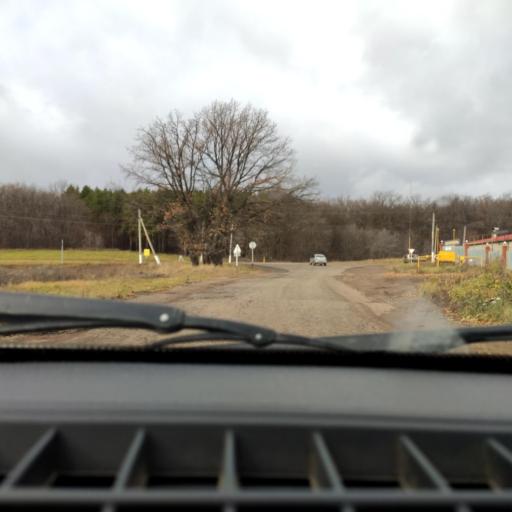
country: RU
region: Bashkortostan
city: Mikhaylovka
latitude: 54.8057
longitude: 55.8774
